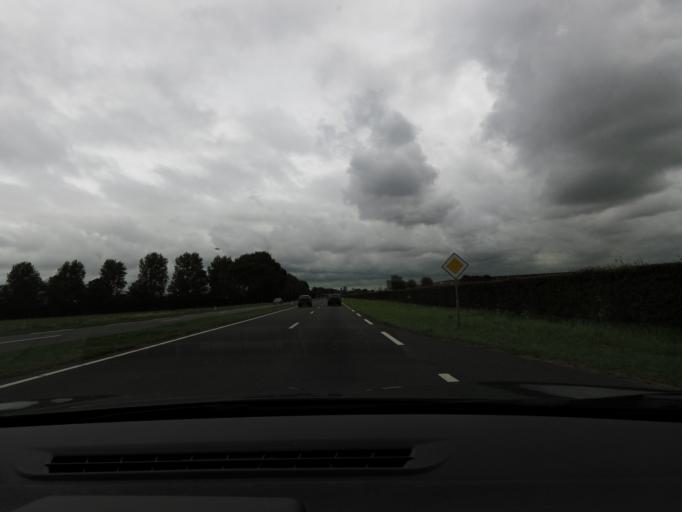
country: NL
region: South Holland
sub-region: Gemeente Spijkenisse
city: Spijkenisse
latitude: 51.8597
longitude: 4.2852
